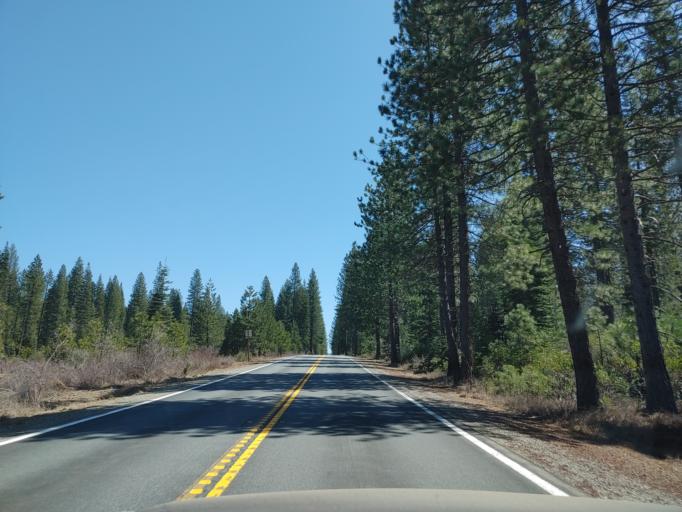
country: US
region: California
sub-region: Siskiyou County
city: McCloud
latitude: 41.2665
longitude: -121.8779
